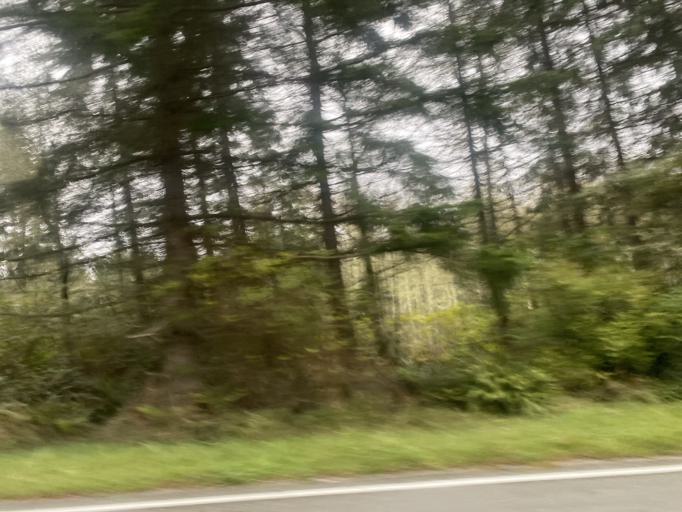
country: US
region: Washington
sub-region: Island County
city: Freeland
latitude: 48.0870
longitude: -122.4989
